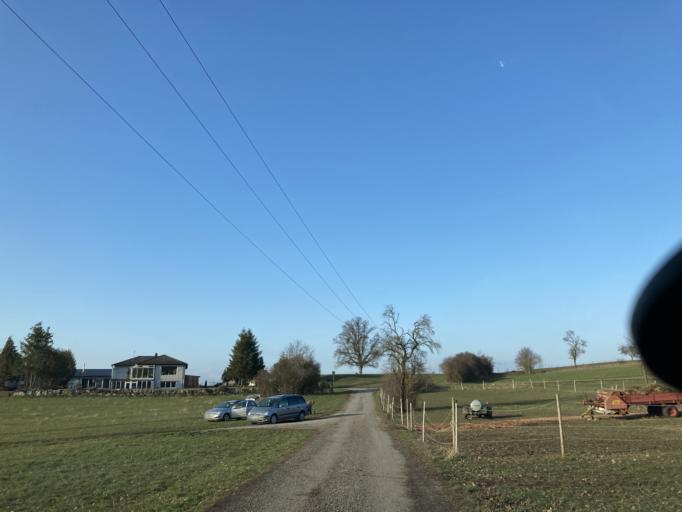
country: DE
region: Baden-Wuerttemberg
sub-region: Tuebingen Region
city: Hirrlingen
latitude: 48.3997
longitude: 8.8899
